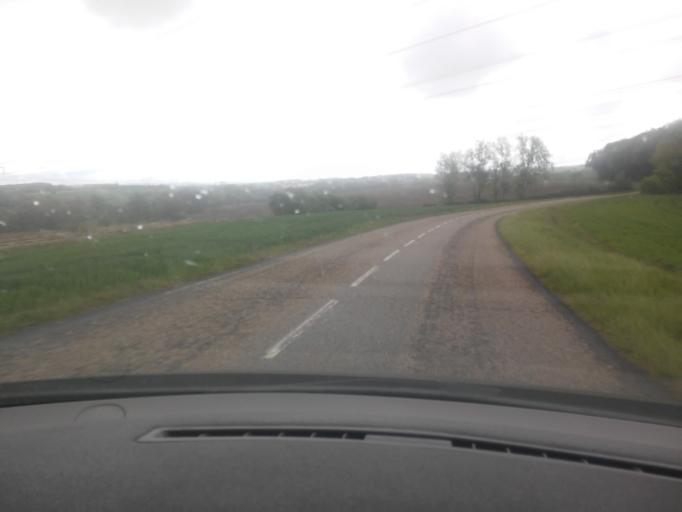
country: FR
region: Lorraine
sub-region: Departement de la Moselle
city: Mecleuves
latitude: 49.0134
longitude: 6.2571
